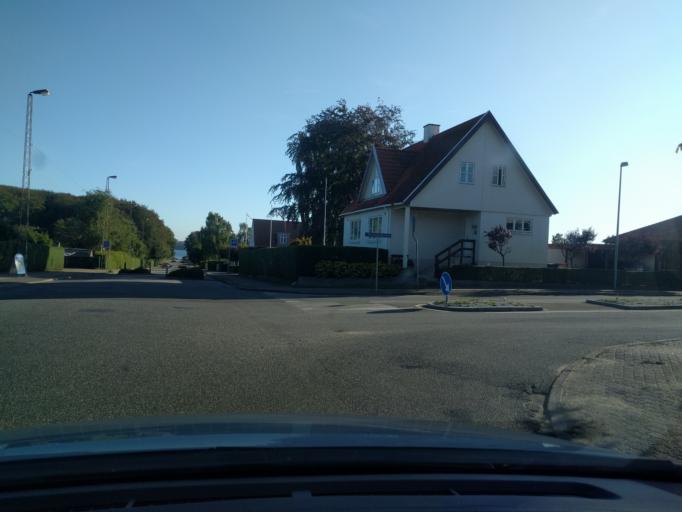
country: DK
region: Central Jutland
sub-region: Horsens Kommune
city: Horsens
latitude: 55.8638
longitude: 9.9160
